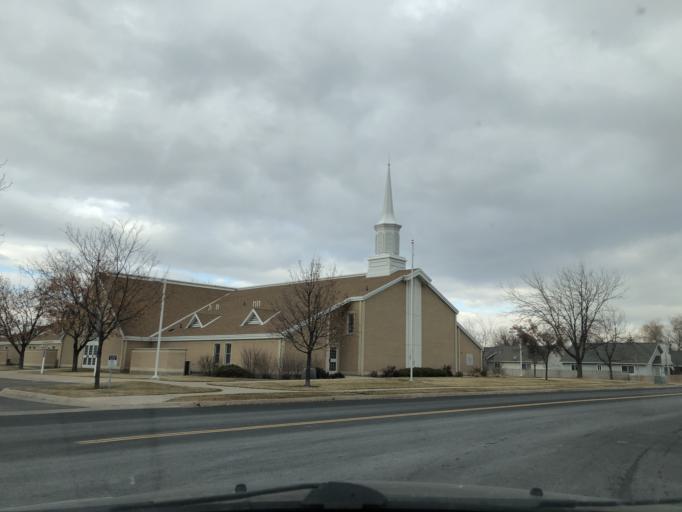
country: US
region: Utah
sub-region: Cache County
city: Logan
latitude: 41.7466
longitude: -111.8395
